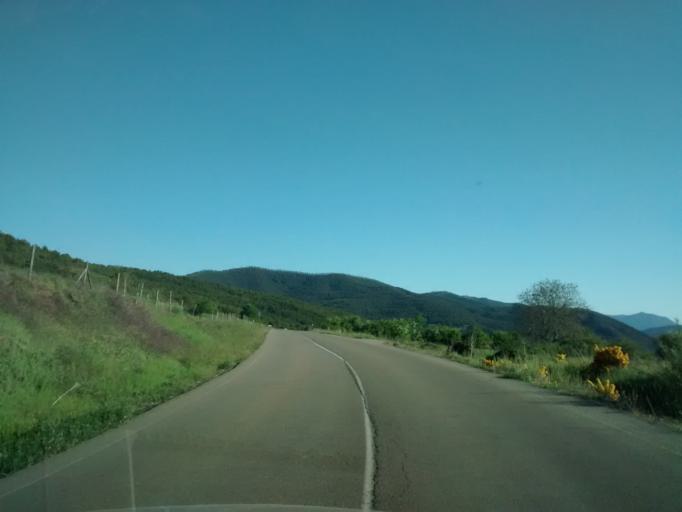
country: ES
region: Aragon
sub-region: Provincia de Huesca
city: Borau
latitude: 42.6752
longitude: -0.6209
